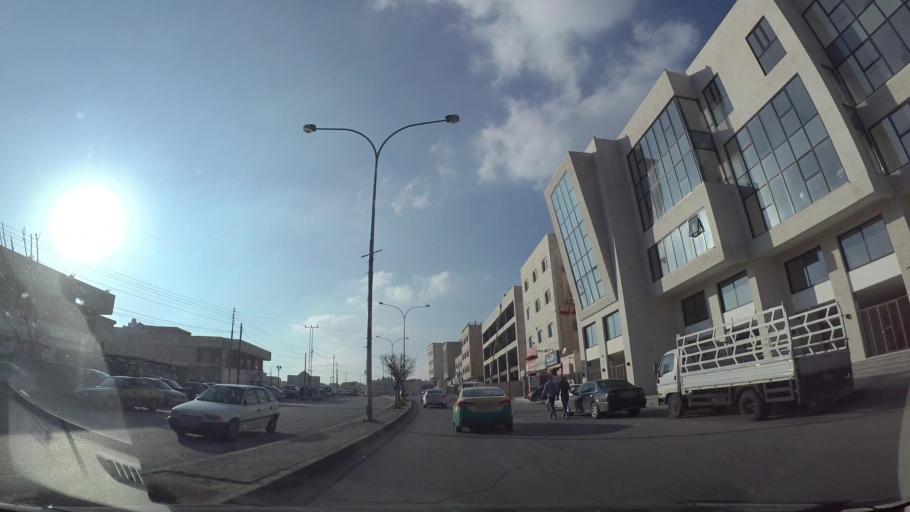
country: JO
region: Amman
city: Amman
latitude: 31.9794
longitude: 35.9424
